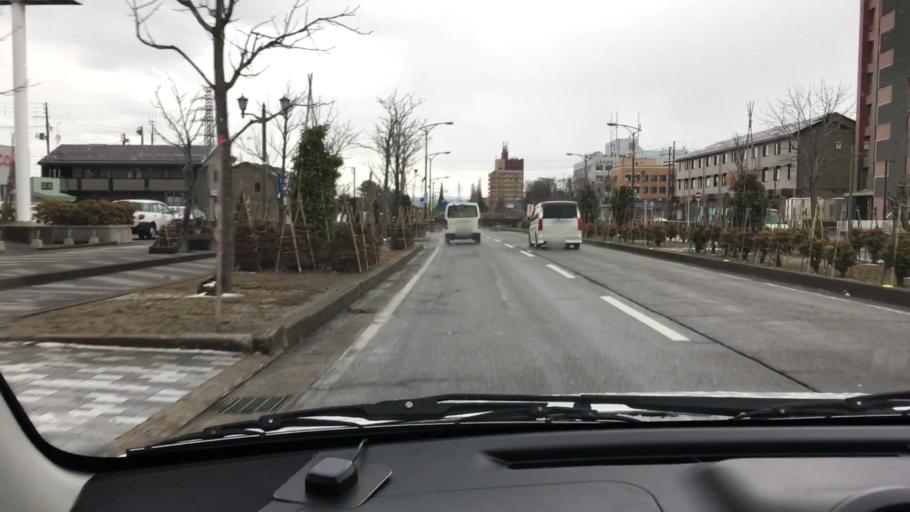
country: JP
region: Niigata
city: Joetsu
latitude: 37.1481
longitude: 138.2320
